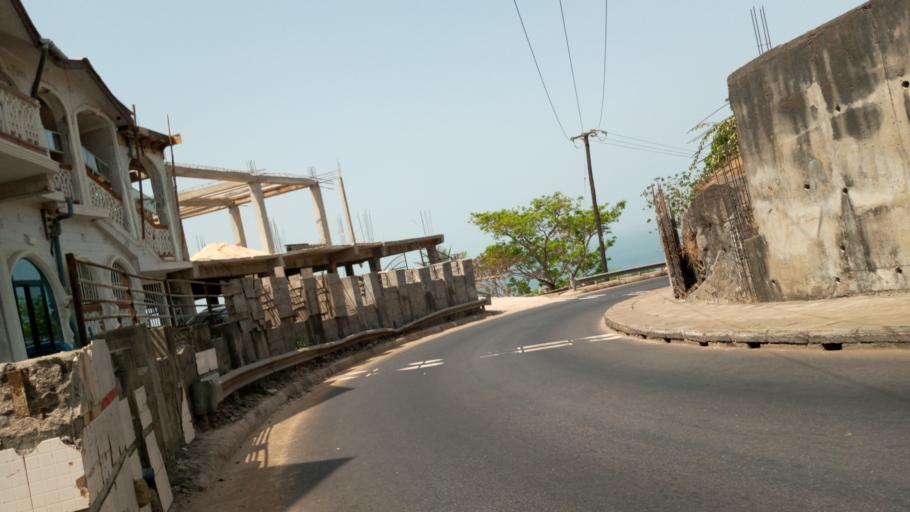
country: SL
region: Western Area
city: Freetown
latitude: 8.4828
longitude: -13.2672
